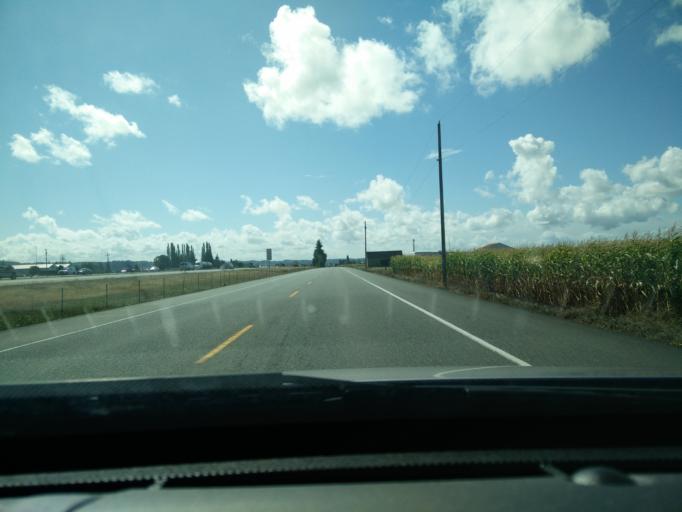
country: US
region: Washington
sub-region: Skagit County
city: Mount Vernon
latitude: 48.3756
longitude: -122.3362
